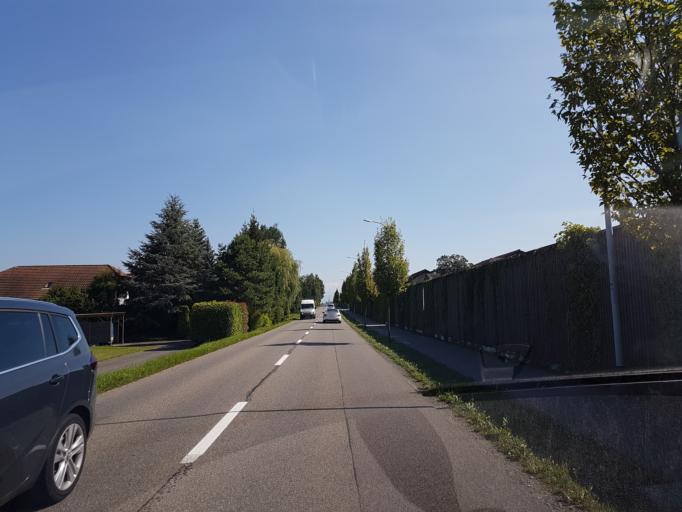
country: CH
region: Aargau
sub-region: Bezirk Muri
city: Buttwil
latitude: 47.2966
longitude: 8.3183
